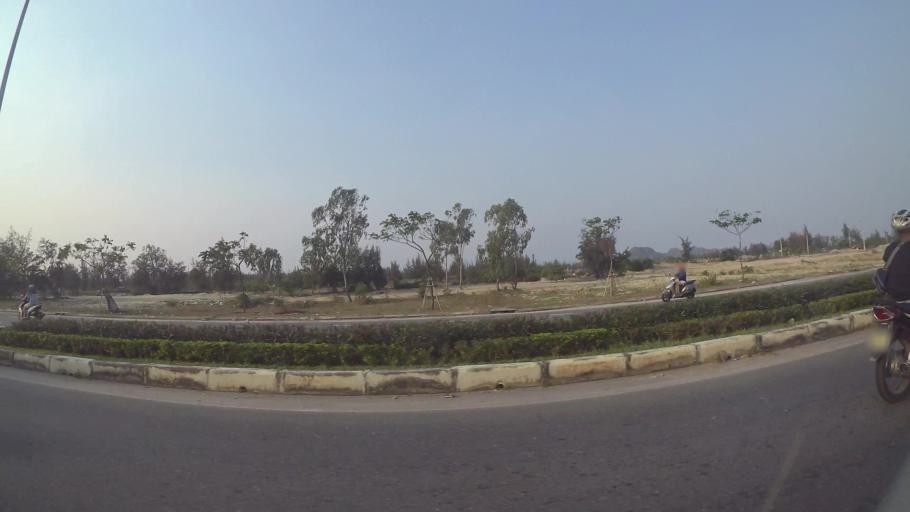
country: VN
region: Da Nang
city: Ngu Hanh Son
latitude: 15.9832
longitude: 108.2450
